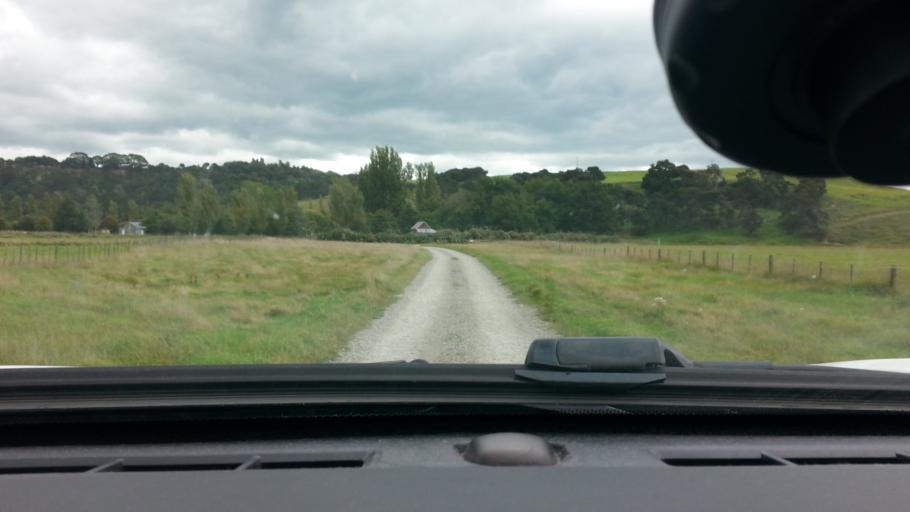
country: NZ
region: Wellington
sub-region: Masterton District
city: Masterton
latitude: -41.1517
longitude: 175.4839
